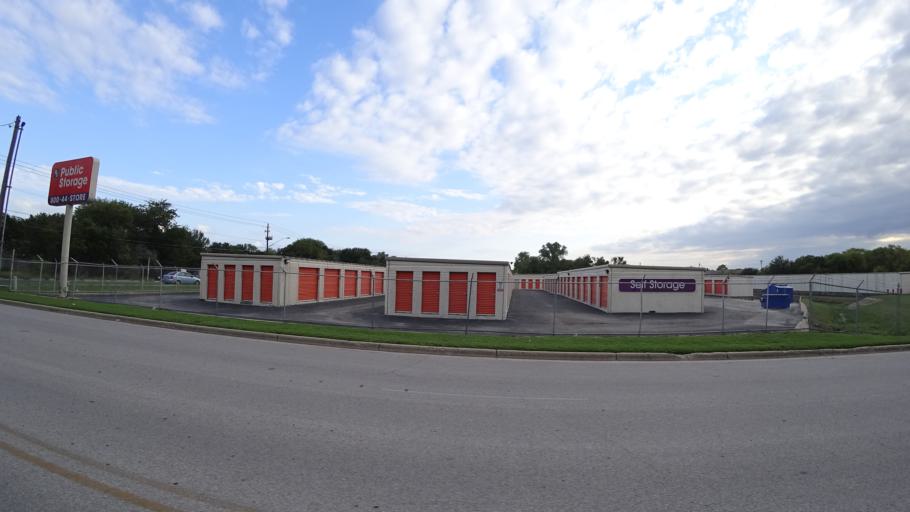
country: US
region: Texas
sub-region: Travis County
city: Onion Creek
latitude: 30.1920
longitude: -97.7908
